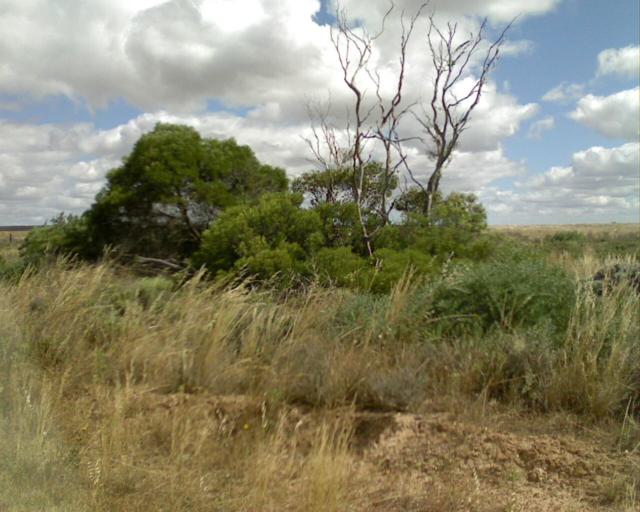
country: AU
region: South Australia
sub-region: Ceduna
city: Ceduna
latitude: -32.0755
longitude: 133.4757
